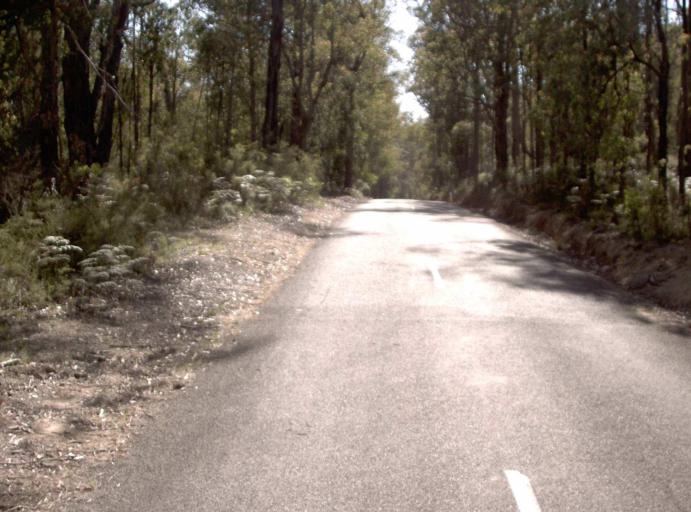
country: AU
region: New South Wales
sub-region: Bombala
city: Bombala
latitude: -37.3873
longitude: 148.6134
